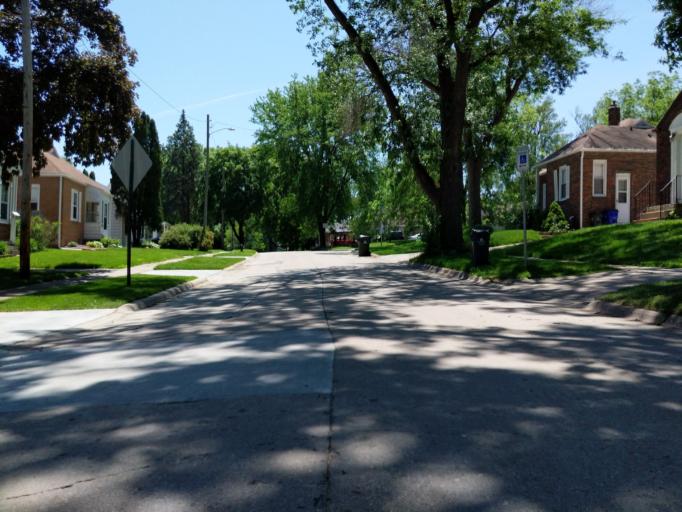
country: US
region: Iowa
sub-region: Linn County
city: Cedar Rapids
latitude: 42.0189
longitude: -91.6362
